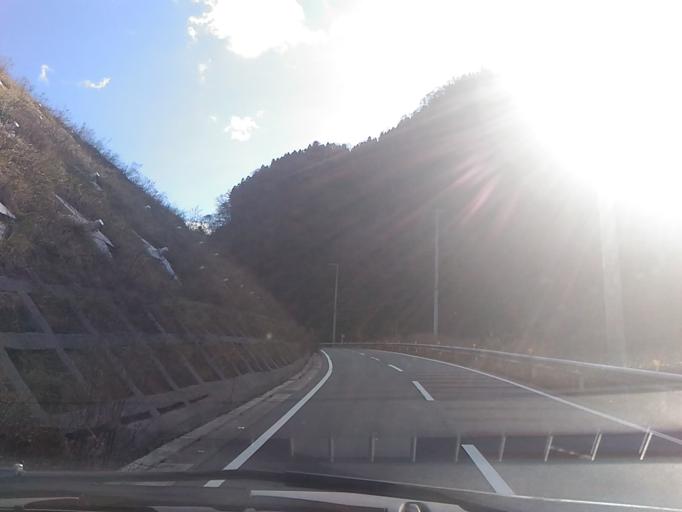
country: JP
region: Fukushima
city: Iwaki
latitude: 37.0122
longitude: 140.6765
